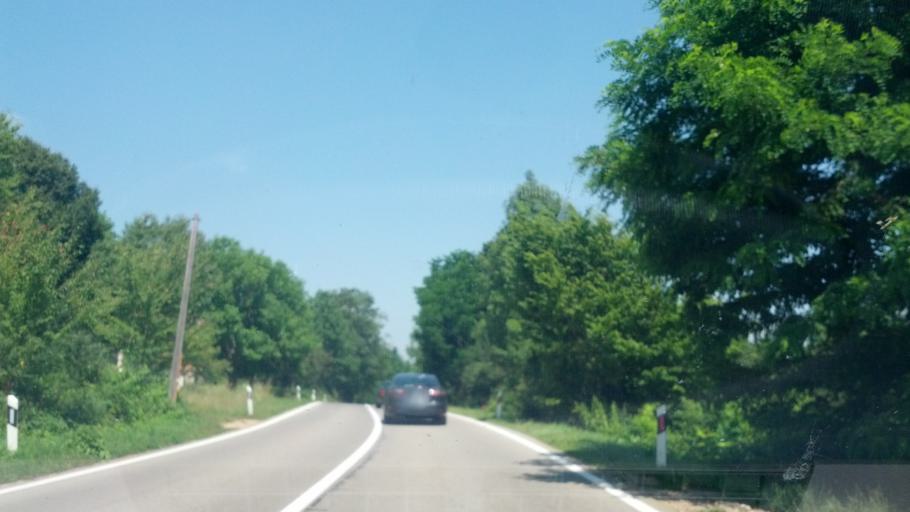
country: BA
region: Federation of Bosnia and Herzegovina
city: Izacic
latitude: 44.8878
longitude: 15.7263
